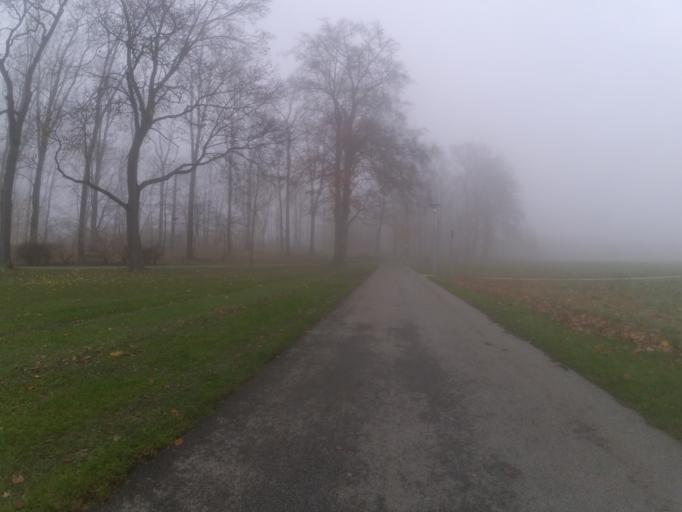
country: DE
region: Bavaria
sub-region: Swabia
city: Neu-Ulm
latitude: 48.3823
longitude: 10.0101
